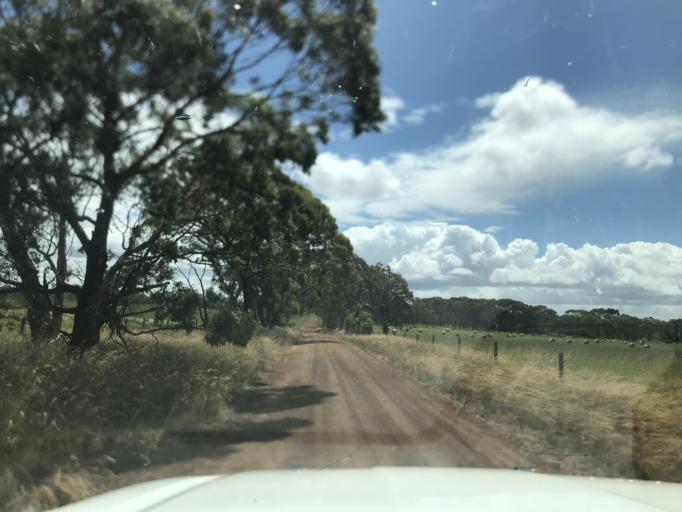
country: AU
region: South Australia
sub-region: Wattle Range
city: Penola
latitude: -37.1238
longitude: 141.2842
